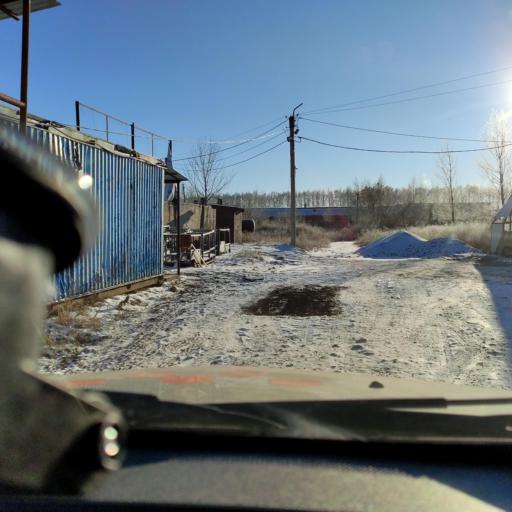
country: RU
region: Bashkortostan
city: Mikhaylovka
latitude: 54.8621
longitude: 55.7477
